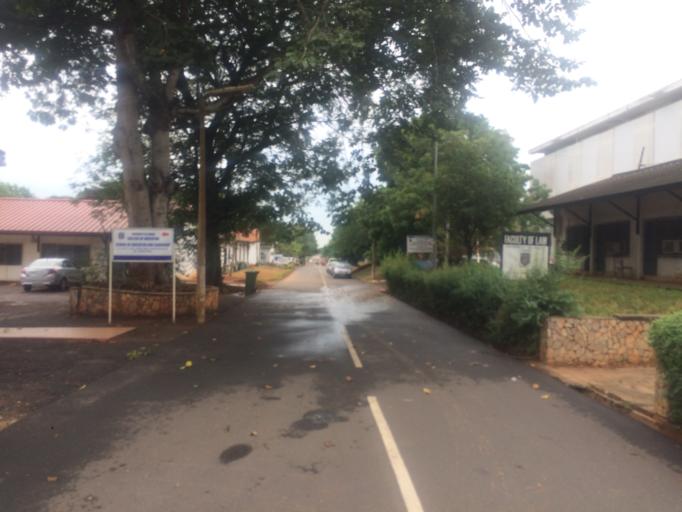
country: GH
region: Greater Accra
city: Medina Estates
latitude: 5.6529
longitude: -0.1814
